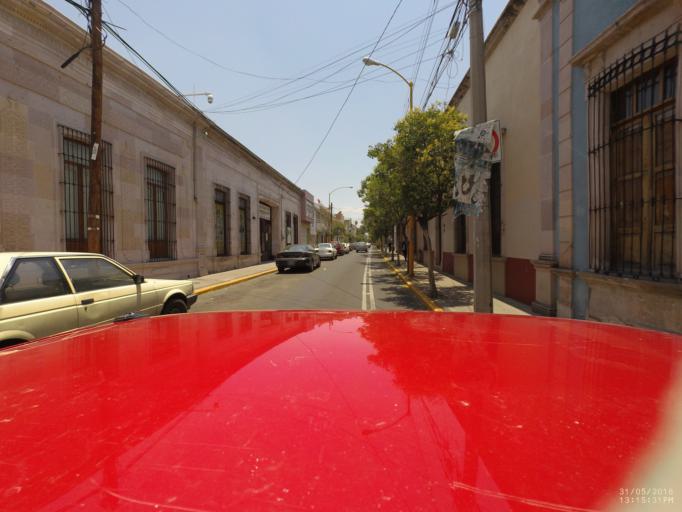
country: MX
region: Aguascalientes
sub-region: Aguascalientes
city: Aguascalientes
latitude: 21.8818
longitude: -102.2897
